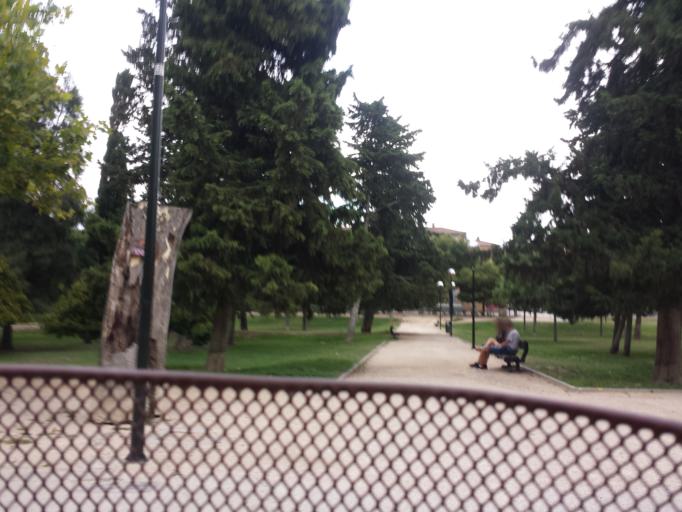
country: ES
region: Aragon
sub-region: Provincia de Zaragoza
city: Zaragoza
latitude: 41.6639
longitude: -0.8766
